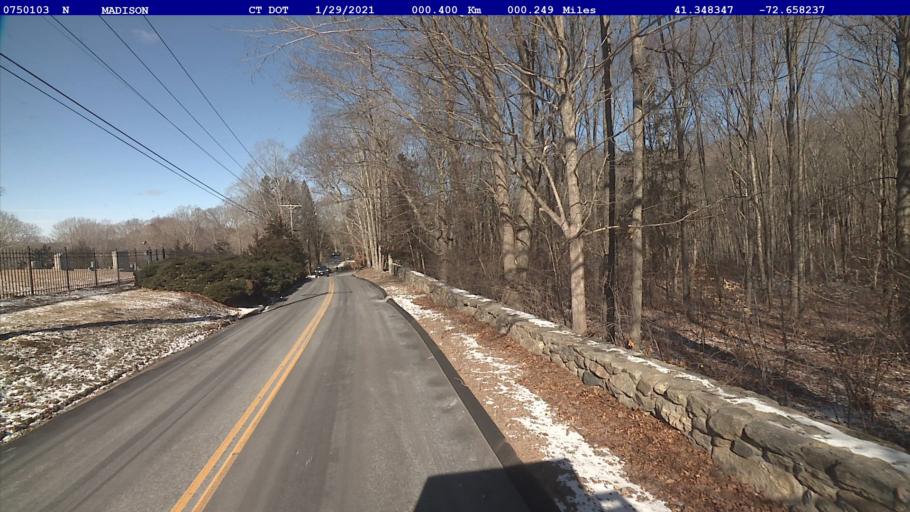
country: US
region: Connecticut
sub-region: New Haven County
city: Guilford
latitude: 41.3484
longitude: -72.6582
